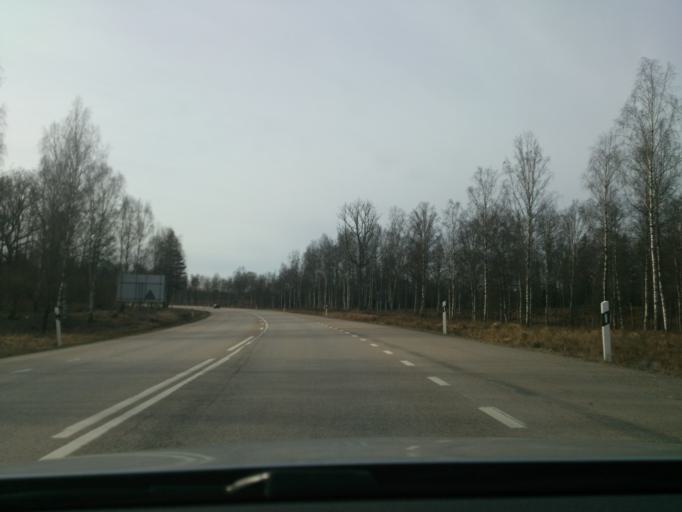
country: SE
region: Kronoberg
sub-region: Alvesta Kommun
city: Alvesta
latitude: 56.9174
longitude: 14.5543
